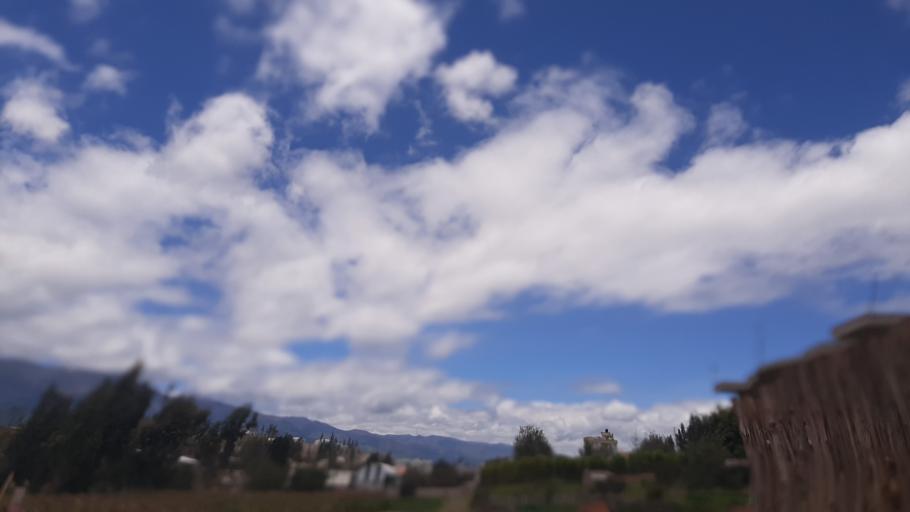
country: EC
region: Chimborazo
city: Riobamba
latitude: -1.6562
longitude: -78.6340
